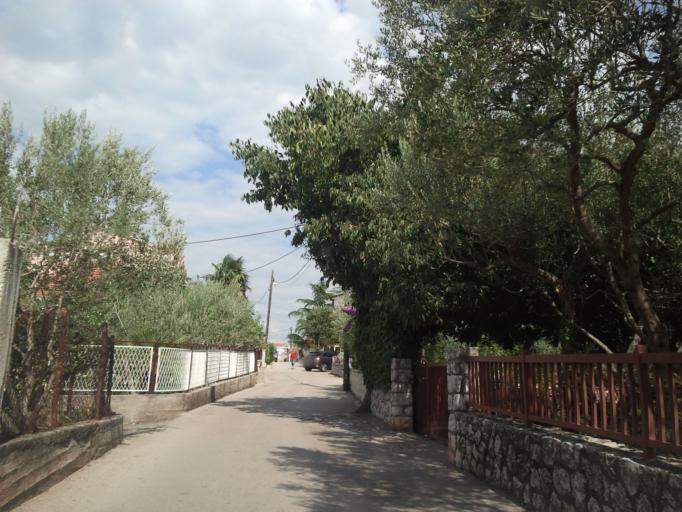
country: HR
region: Zadarska
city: Zadar
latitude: 44.1188
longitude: 15.2494
